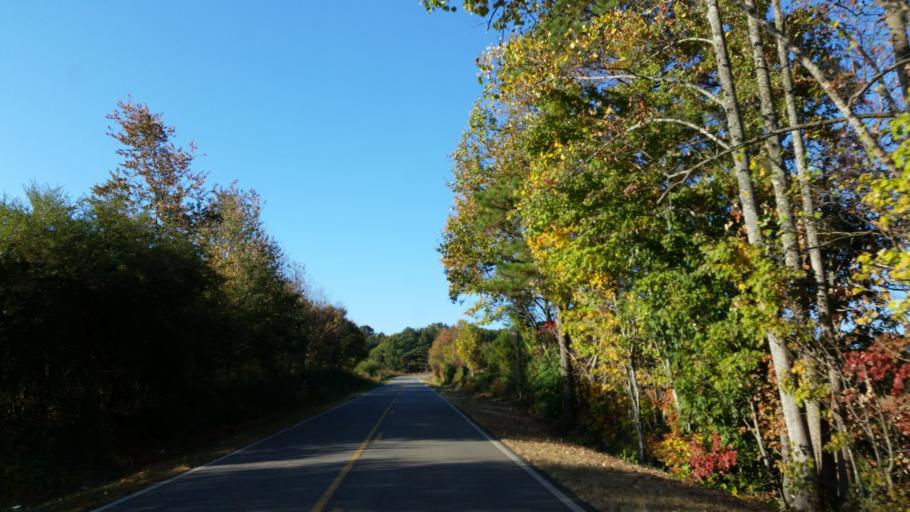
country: US
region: Georgia
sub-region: Gilmer County
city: Ellijay
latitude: 34.5861
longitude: -84.4573
